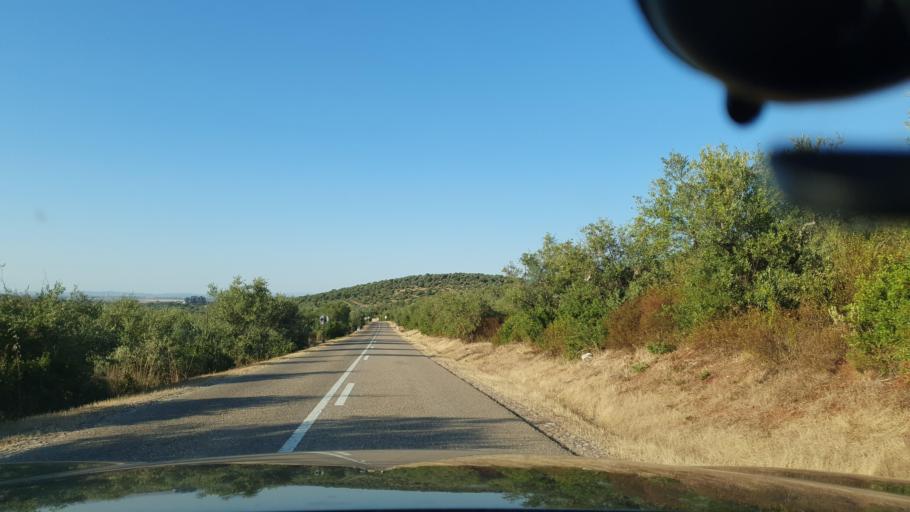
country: PT
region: Evora
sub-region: Estremoz
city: Estremoz
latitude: 38.9230
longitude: -7.6669
